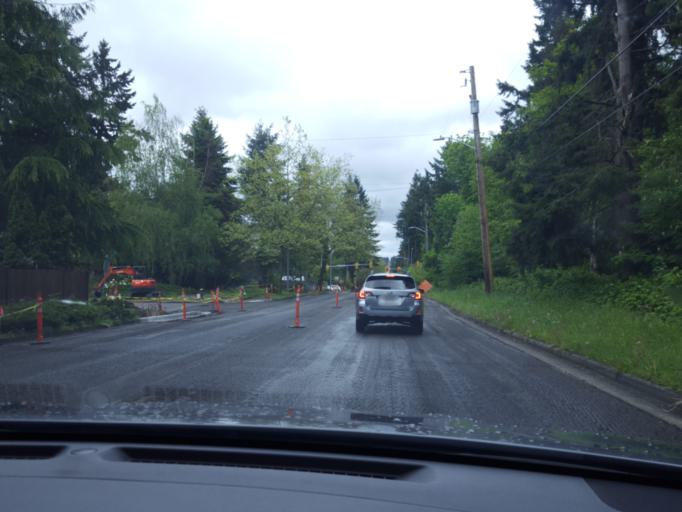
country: US
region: Washington
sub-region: King County
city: Shoreline
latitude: 47.7727
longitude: -122.3352
